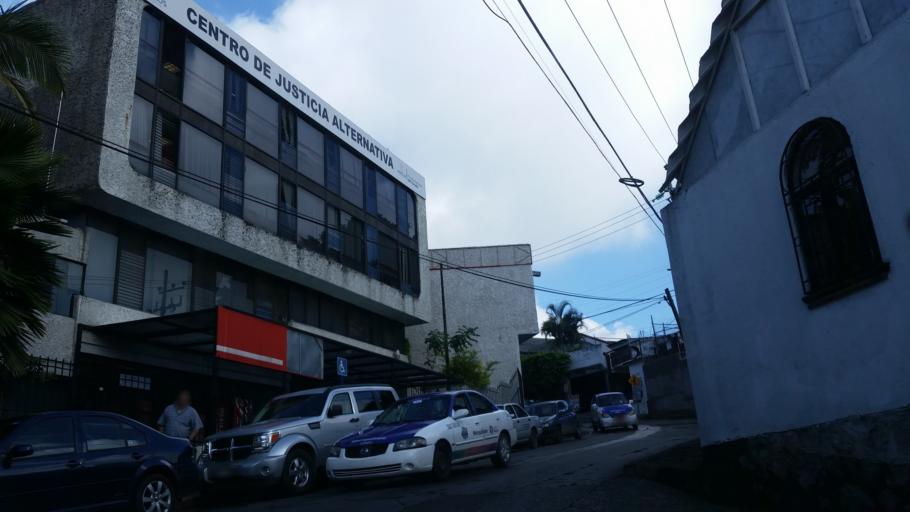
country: MX
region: Morelos
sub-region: Cuernavaca
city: Cuernavaca
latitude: 18.9200
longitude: -99.2102
